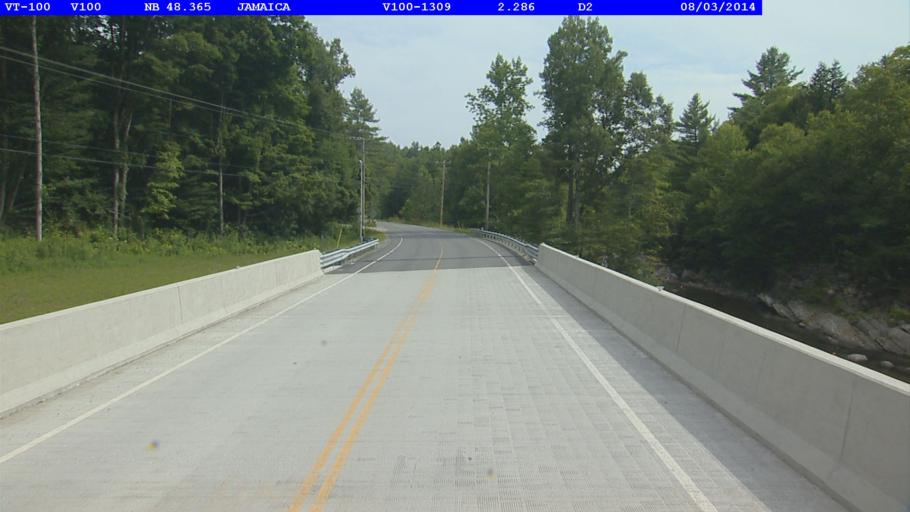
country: US
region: Vermont
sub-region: Windham County
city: Newfane
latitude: 43.0662
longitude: -72.7534
